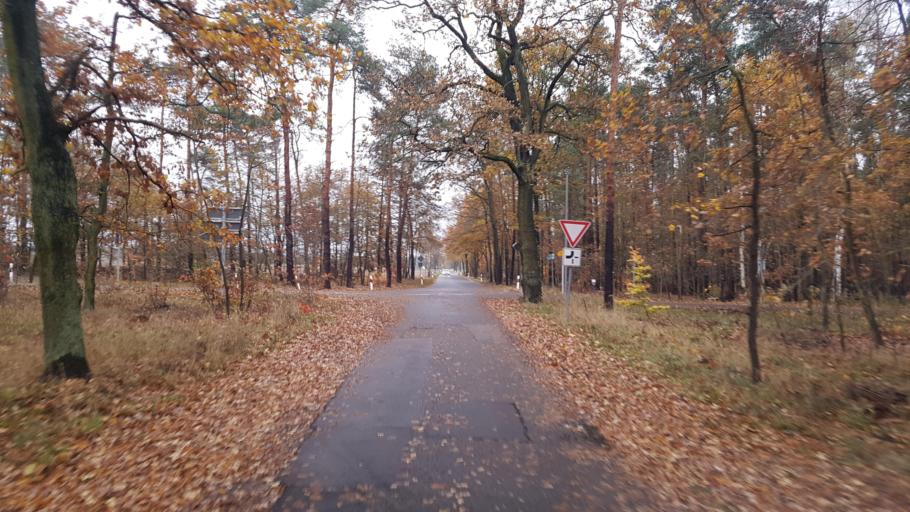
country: DE
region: Brandenburg
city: Drebkau
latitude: 51.6943
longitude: 14.1974
